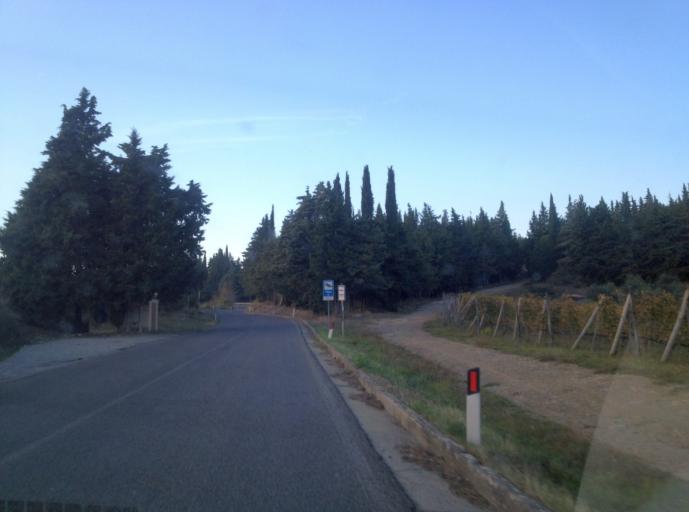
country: IT
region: Tuscany
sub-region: Provincia di Siena
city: Castellina in Chianti
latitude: 43.4464
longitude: 11.2991
